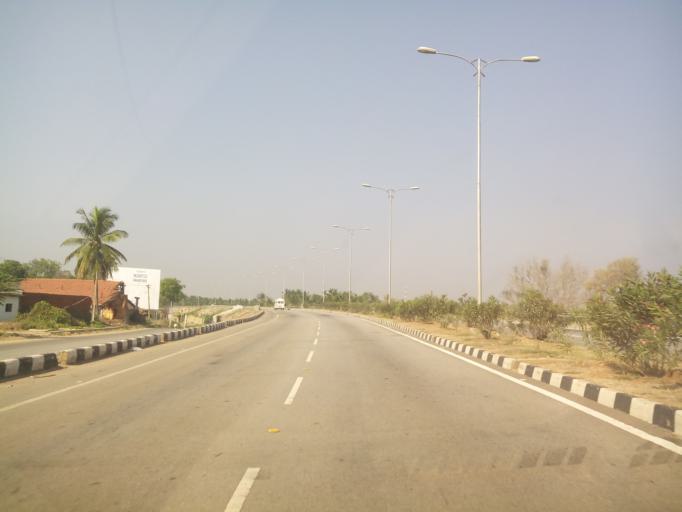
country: IN
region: Karnataka
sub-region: Tumkur
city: Kunigal
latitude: 13.0301
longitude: 77.0790
